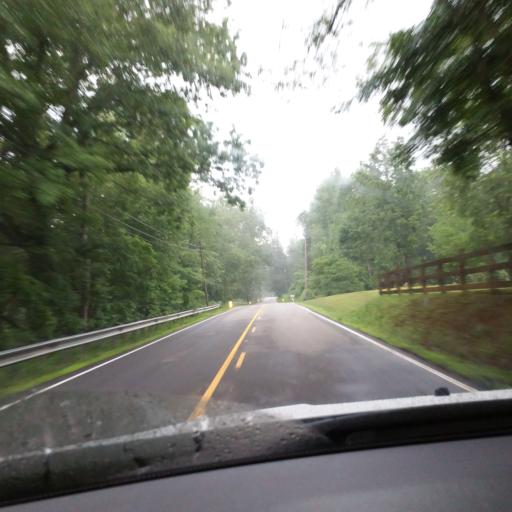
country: US
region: North Carolina
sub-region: Yancey County
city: Burnsville
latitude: 35.8244
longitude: -82.1895
